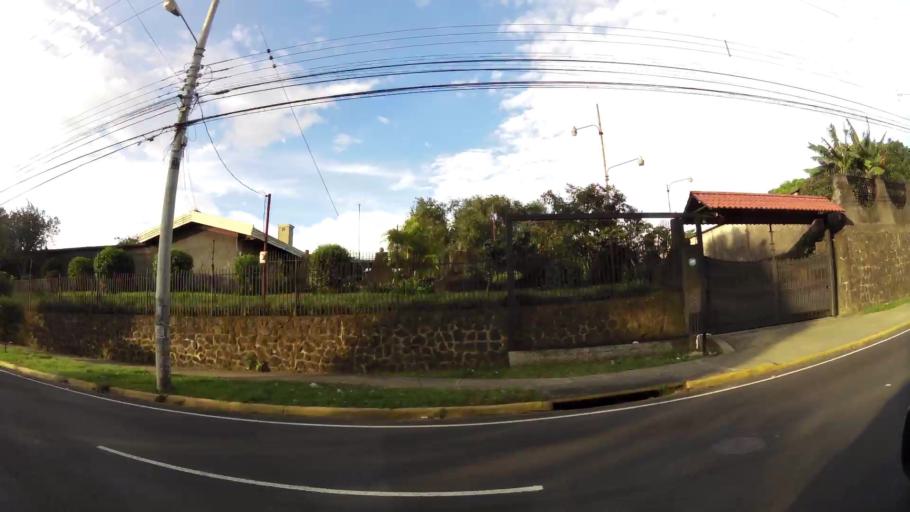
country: CR
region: Heredia
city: San Francisco
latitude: 9.9962
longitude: -84.1306
